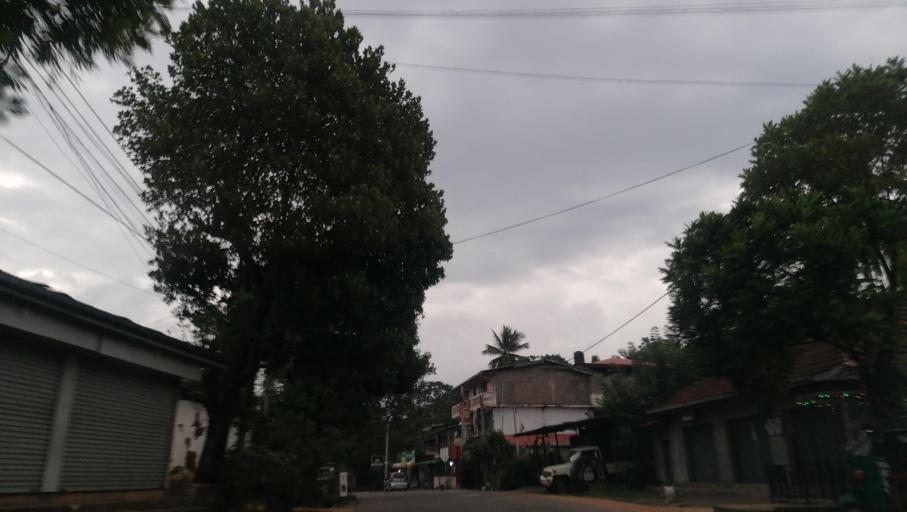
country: LK
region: Central
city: Kandy
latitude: 7.2144
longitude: 80.7825
